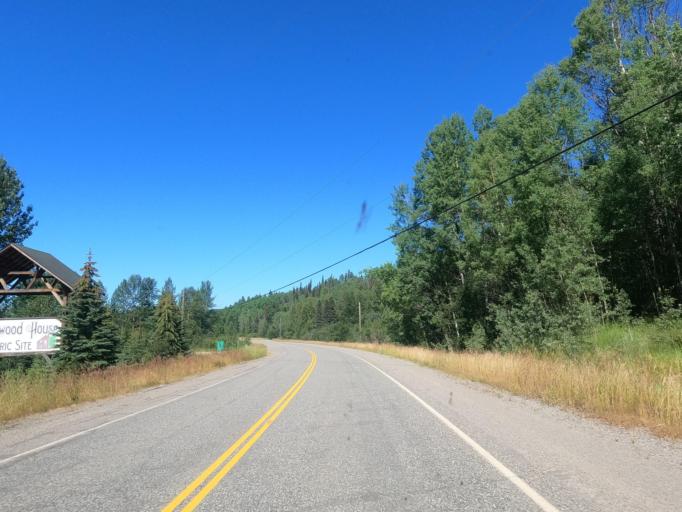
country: CA
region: British Columbia
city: Quesnel
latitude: 53.0524
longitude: -122.1559
